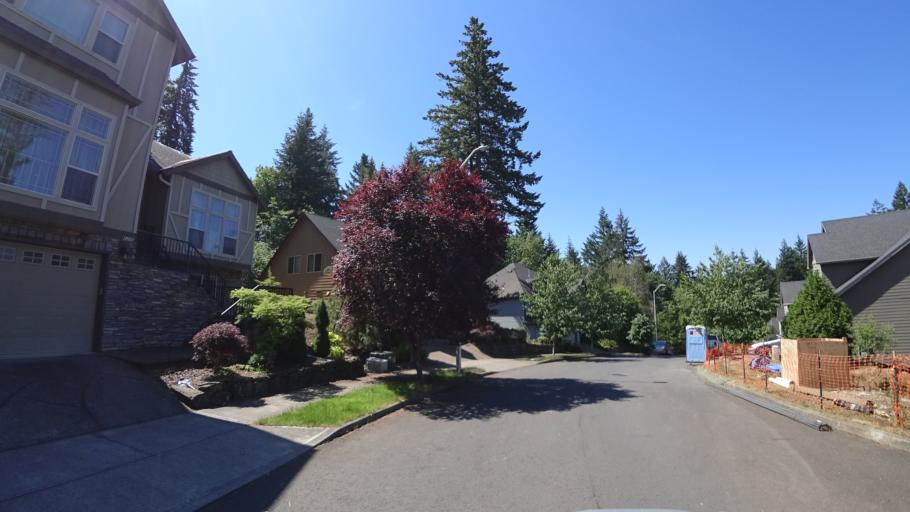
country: US
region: Oregon
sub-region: Clackamas County
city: Happy Valley
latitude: 45.4632
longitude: -122.5205
